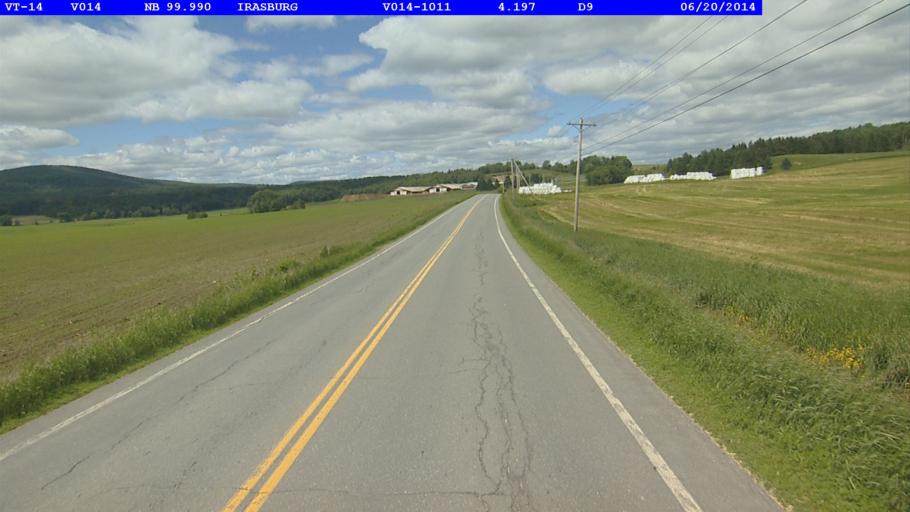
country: US
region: Vermont
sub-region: Orleans County
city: Newport
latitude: 44.8203
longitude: -72.2952
